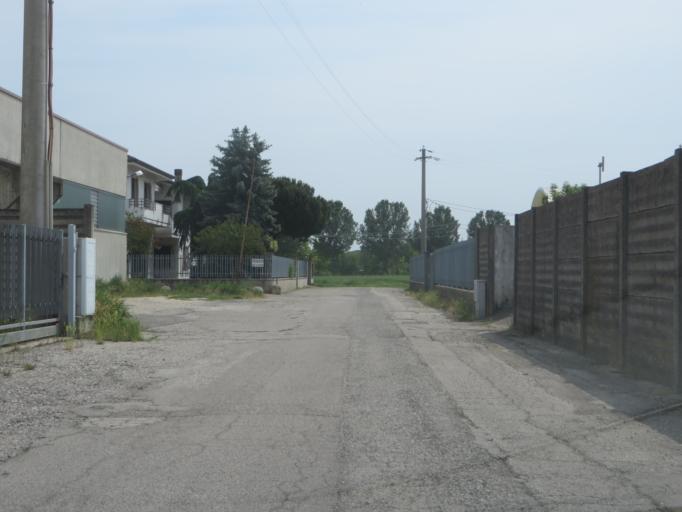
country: IT
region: Veneto
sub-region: Provincia di Verona
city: Legnago
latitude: 45.1885
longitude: 11.2874
